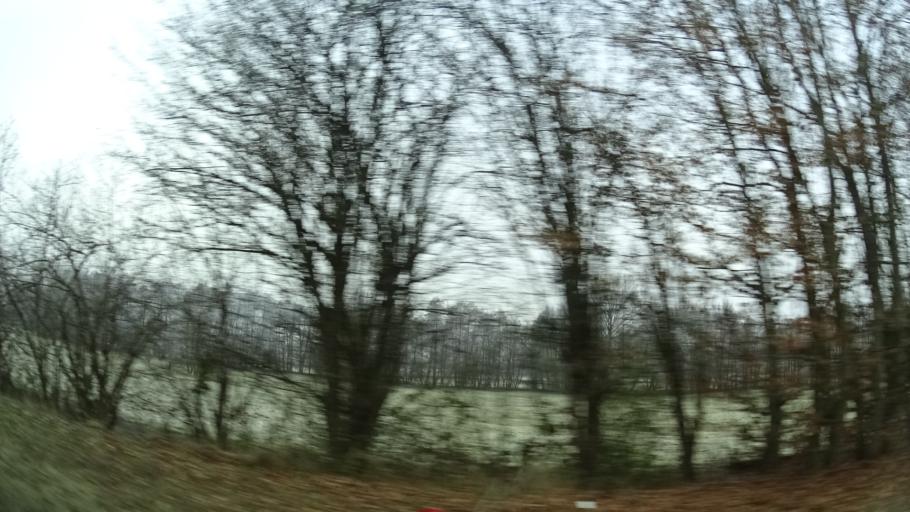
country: DE
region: Bavaria
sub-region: Regierungsbezirk Unterfranken
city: Blankenbach
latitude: 50.0611
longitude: 9.2284
